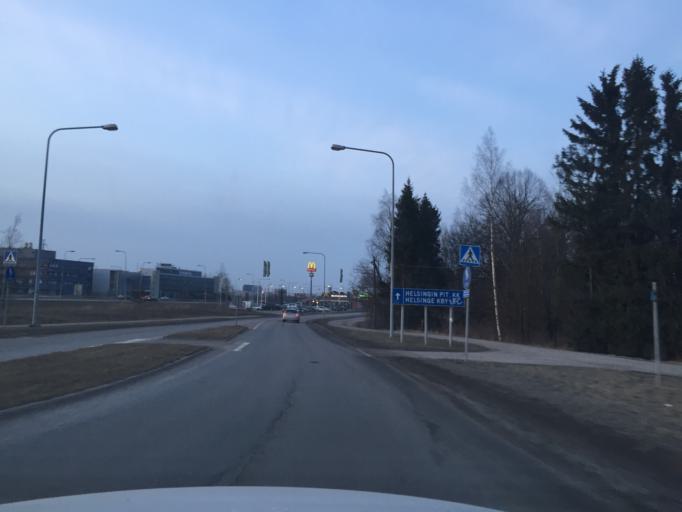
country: FI
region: Uusimaa
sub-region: Helsinki
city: Vantaa
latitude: 60.2688
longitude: 24.9746
